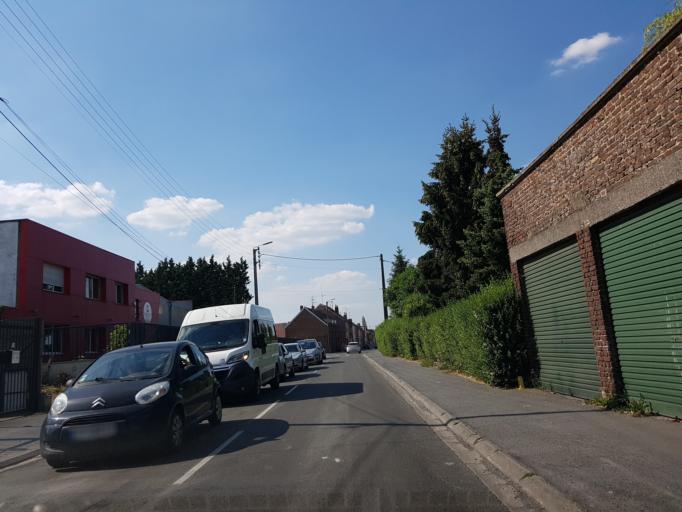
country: FR
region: Nord-Pas-de-Calais
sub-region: Departement du Nord
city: Lourches
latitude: 50.3130
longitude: 3.3444
